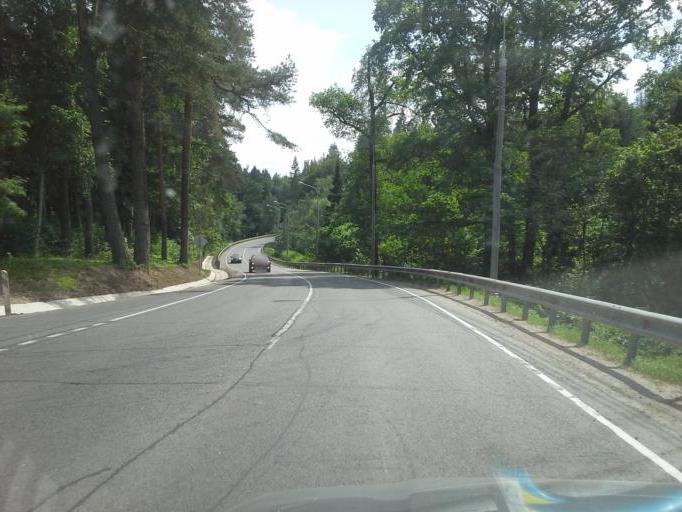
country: RU
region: Moskovskaya
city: Odintsovo
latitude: 55.7082
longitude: 37.2703
